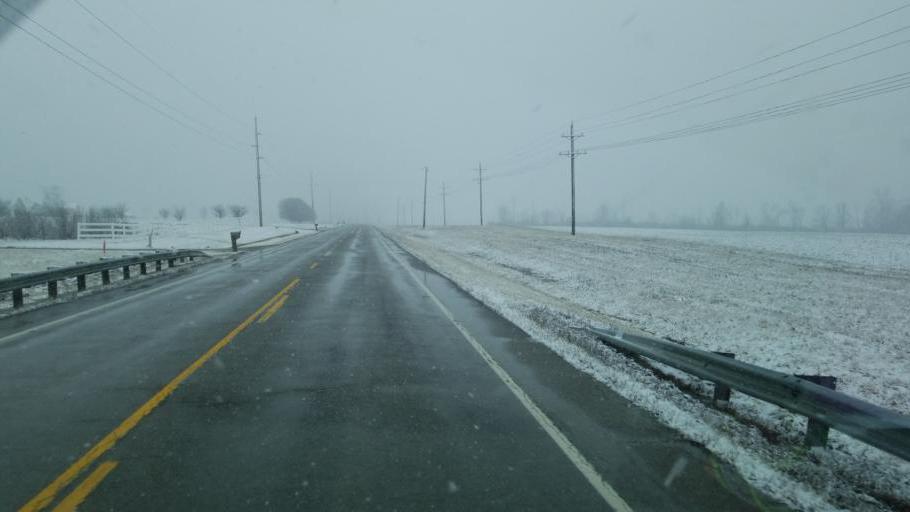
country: US
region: Ohio
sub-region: Champaign County
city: North Lewisburg
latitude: 40.3064
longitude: -83.5164
